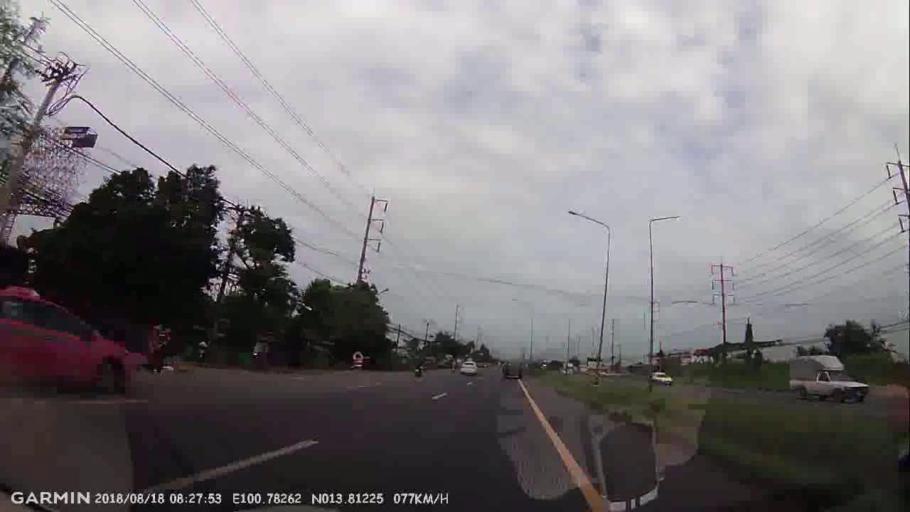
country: TH
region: Bangkok
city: Min Buri
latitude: 13.8123
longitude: 100.7824
